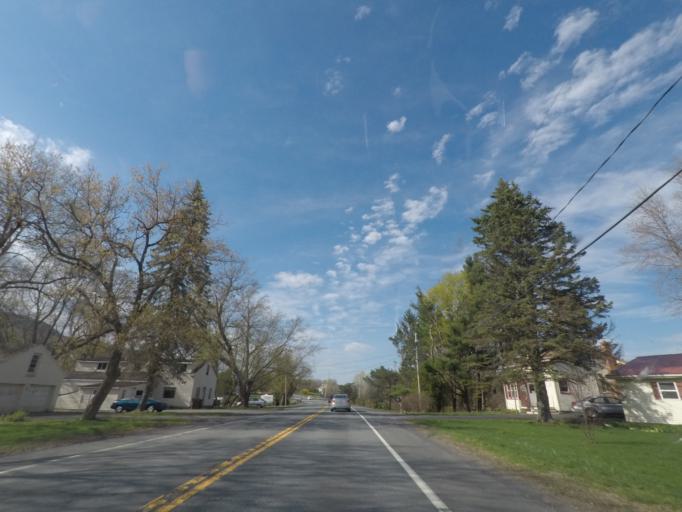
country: US
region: New York
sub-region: Albany County
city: Voorheesville
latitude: 42.6094
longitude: -73.9713
